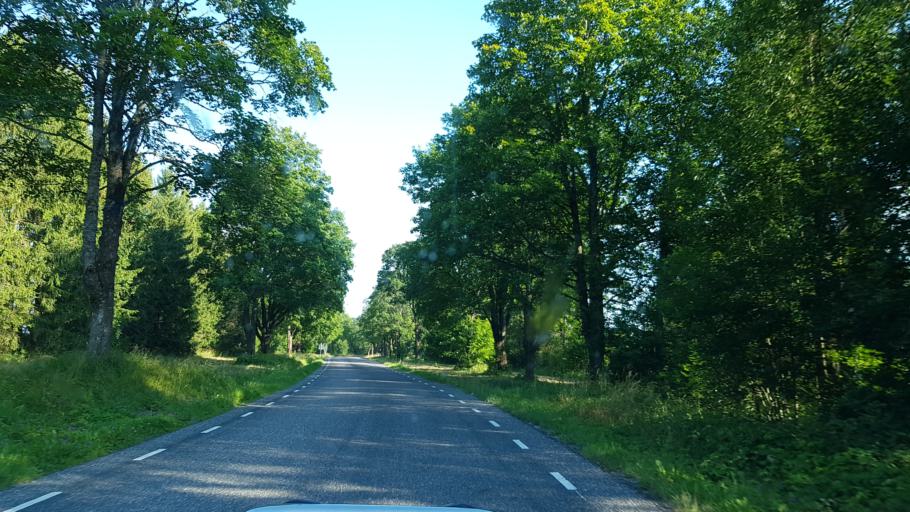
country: EE
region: Polvamaa
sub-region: Polva linn
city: Polva
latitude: 58.0128
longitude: 26.9233
